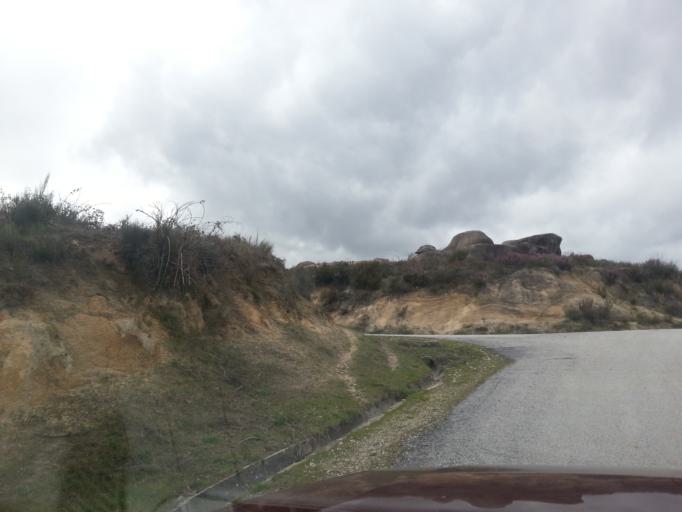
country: PT
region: Guarda
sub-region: Fornos de Algodres
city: Fornos de Algodres
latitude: 40.5882
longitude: -7.5677
